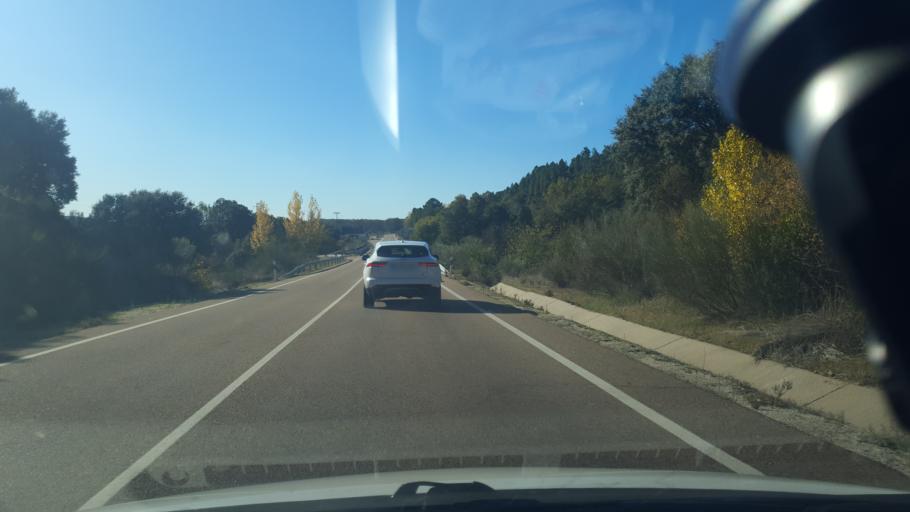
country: ES
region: Castille and Leon
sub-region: Provincia de Avila
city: Arenas de San Pedro
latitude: 40.1828
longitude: -5.0855
